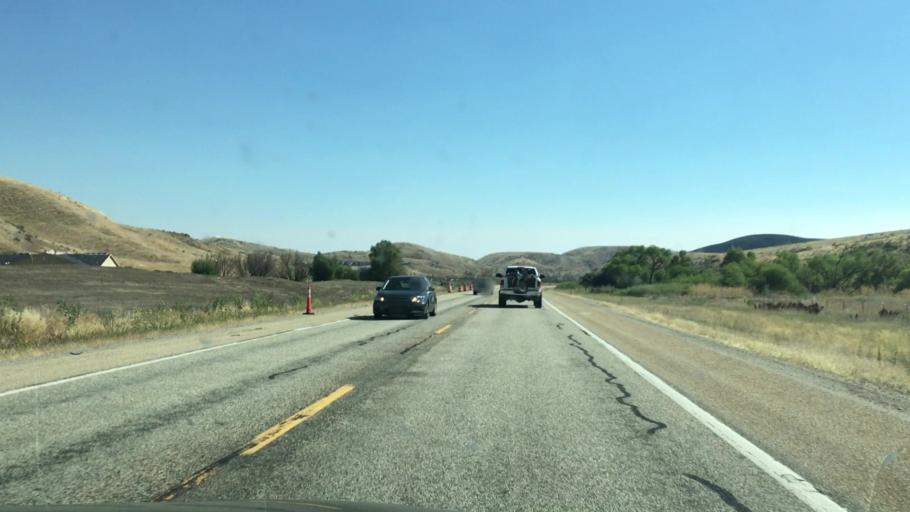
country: US
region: Idaho
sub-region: Ada County
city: Eagle
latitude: 43.7864
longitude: -116.2633
